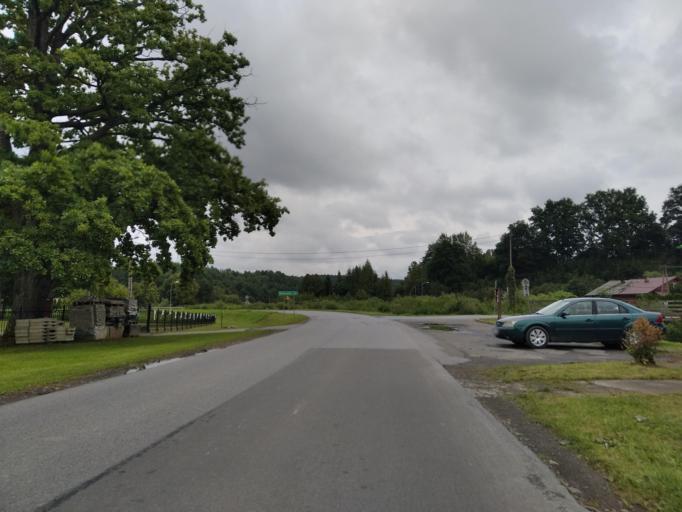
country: PL
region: Subcarpathian Voivodeship
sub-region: Powiat przemyski
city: Bircza
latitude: 49.6802
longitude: 22.4083
